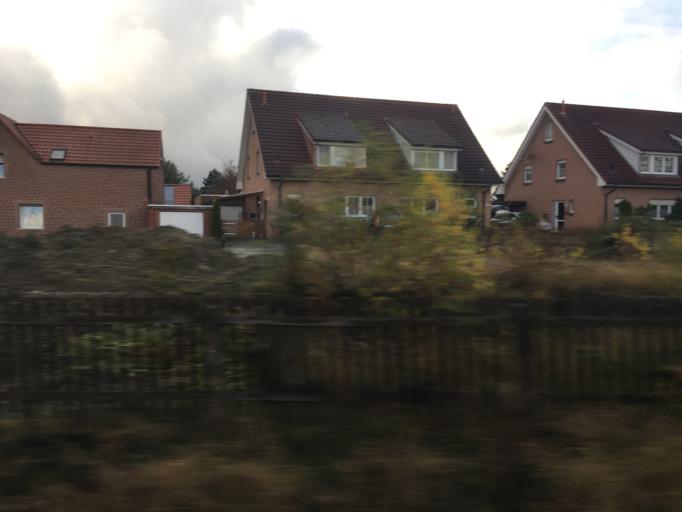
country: DE
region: North Rhine-Westphalia
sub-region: Regierungsbezirk Munster
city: Altenberge
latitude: 52.0551
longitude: 7.4791
